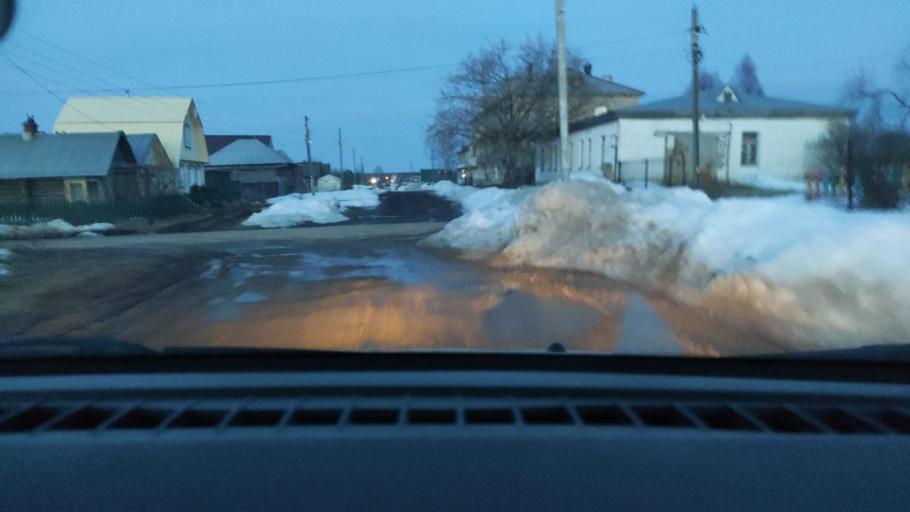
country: RU
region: Perm
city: Yug
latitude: 57.7281
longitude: 56.1661
